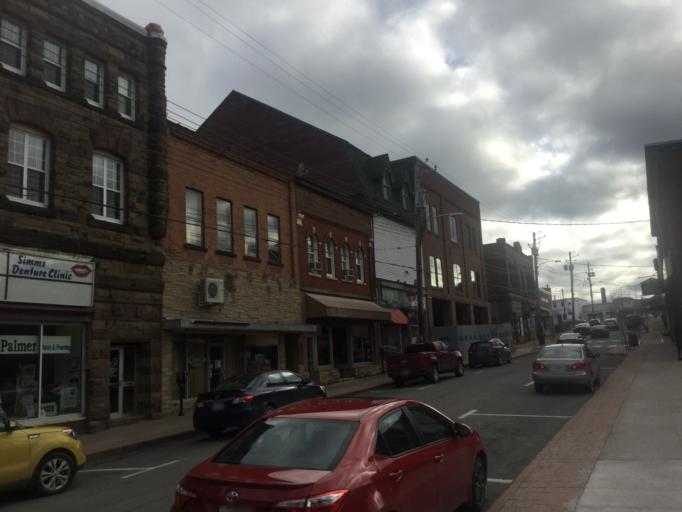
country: CA
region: Nova Scotia
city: New Glasgow
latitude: 45.5871
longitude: -62.6453
